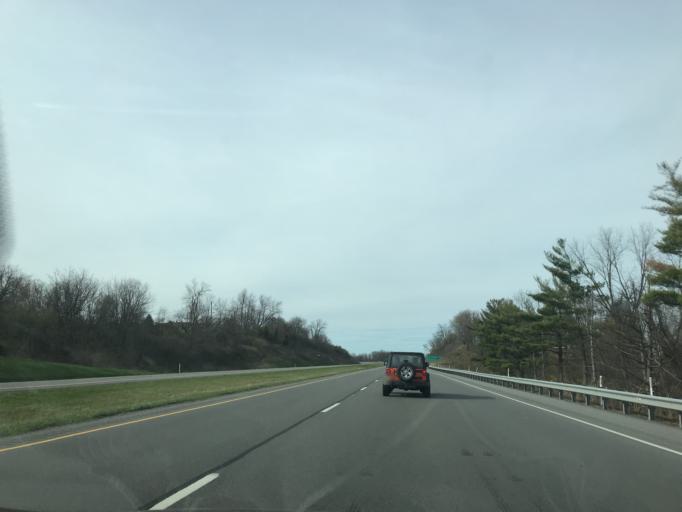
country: US
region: Pennsylvania
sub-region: Union County
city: New Columbia
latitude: 41.0275
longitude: -76.8677
